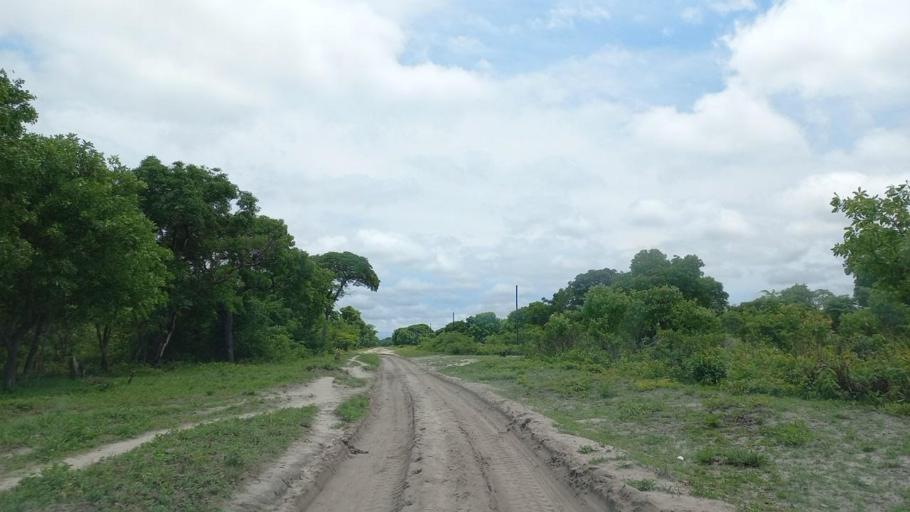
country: ZM
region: North-Western
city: Kabompo
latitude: -13.1847
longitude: 23.9533
